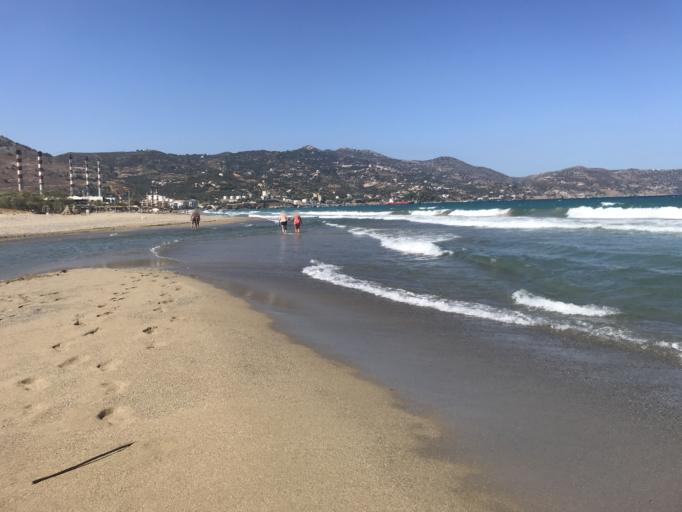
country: GR
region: Crete
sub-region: Nomos Irakleiou
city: Gazi
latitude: 35.3395
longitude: 25.0625
